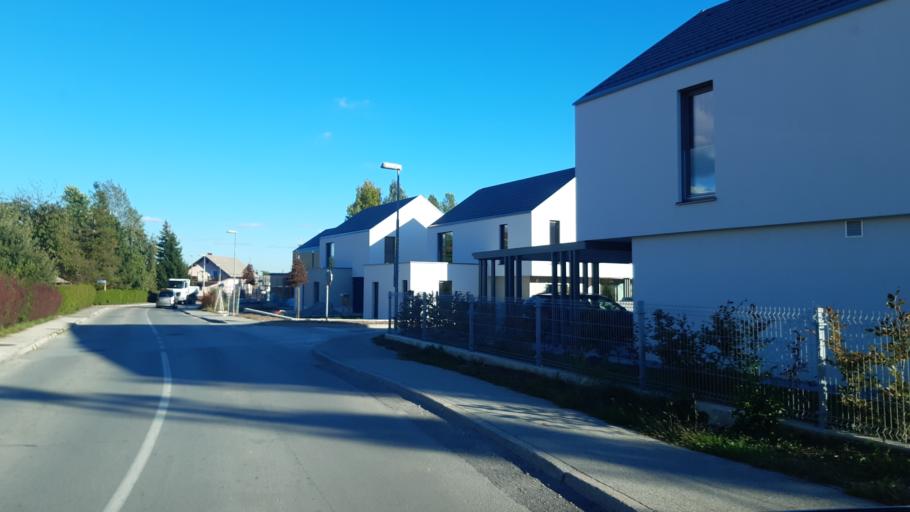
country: SI
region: Kranj
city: Zgornje Bitnje
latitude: 46.2291
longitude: 14.3376
